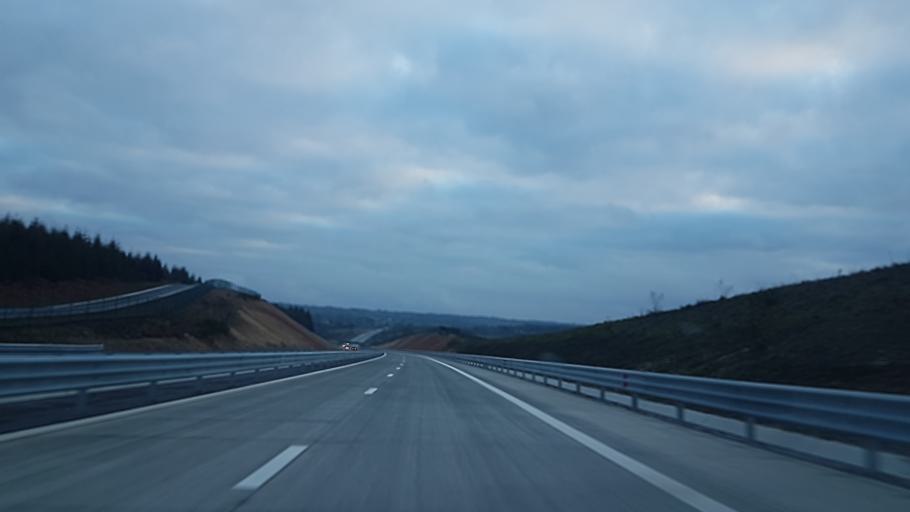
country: FR
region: Champagne-Ardenne
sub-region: Departement des Ardennes
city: Rocroi
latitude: 49.9855
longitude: 4.5399
